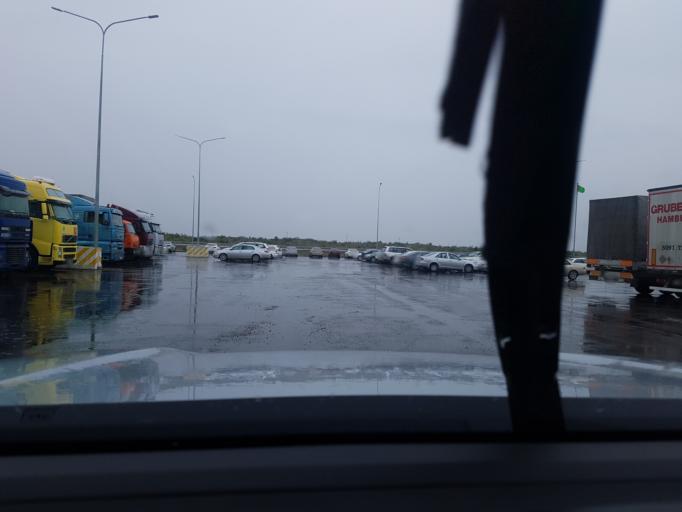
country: TM
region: Lebap
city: Farap
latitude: 39.2060
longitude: 63.6978
